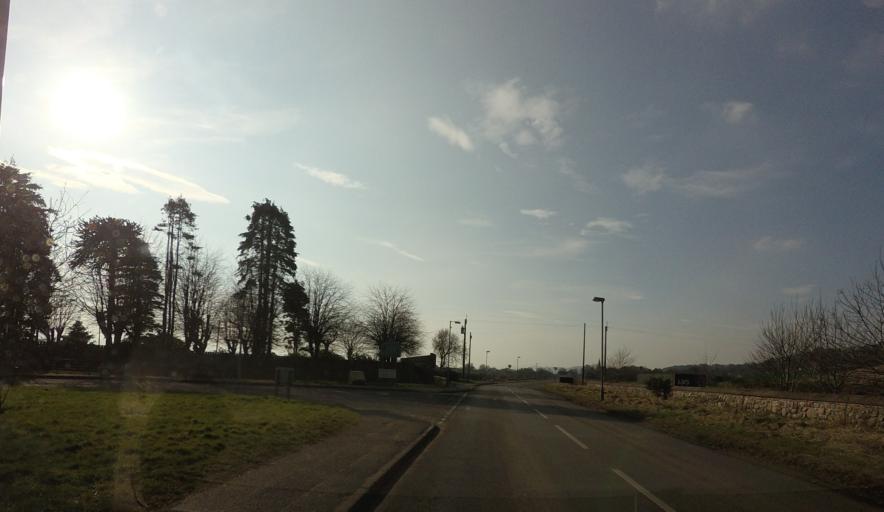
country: GB
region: Scotland
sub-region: Highland
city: Fortrose
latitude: 57.5870
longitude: -4.1208
